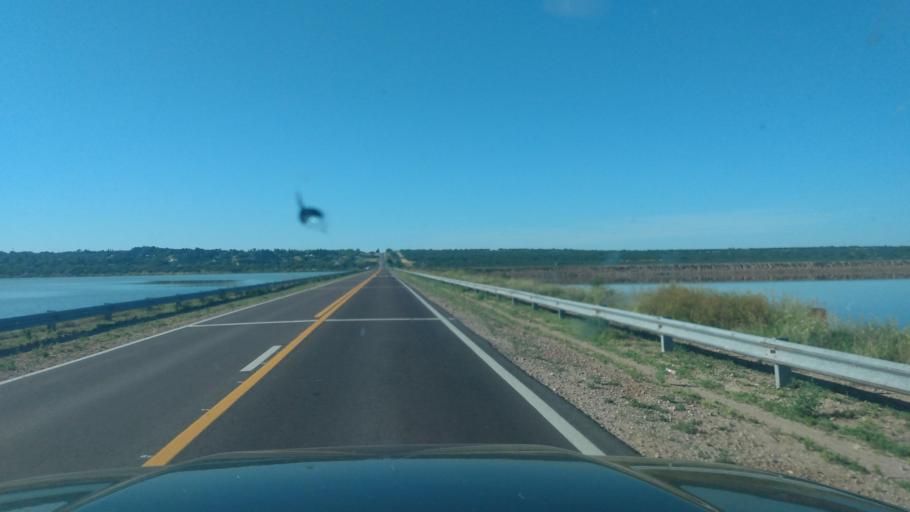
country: AR
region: La Pampa
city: Santa Rosa
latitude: -36.7114
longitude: -64.2831
